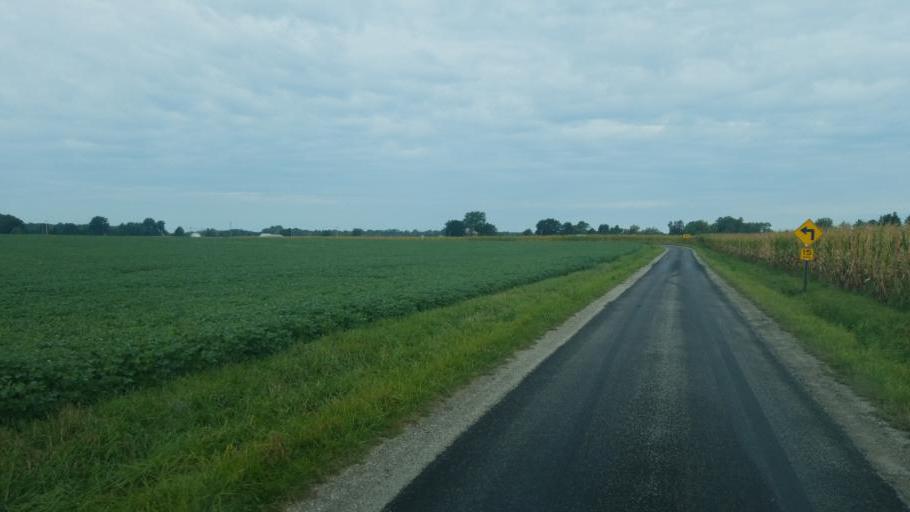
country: US
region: Ohio
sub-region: Crawford County
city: Bucyrus
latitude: 40.7143
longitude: -82.9145
